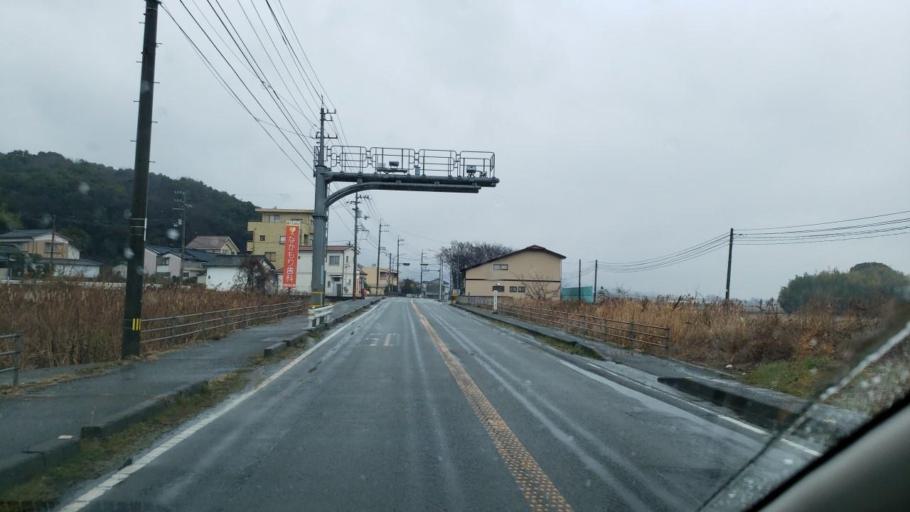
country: JP
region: Tokushima
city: Ishii
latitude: 34.1484
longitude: 134.4825
